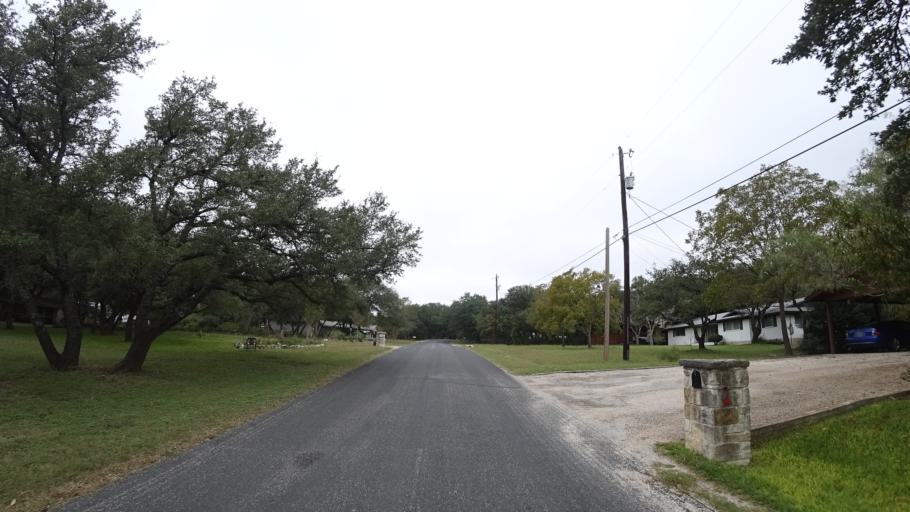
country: US
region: Texas
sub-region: Travis County
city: Barton Creek
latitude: 30.2354
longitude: -97.9010
